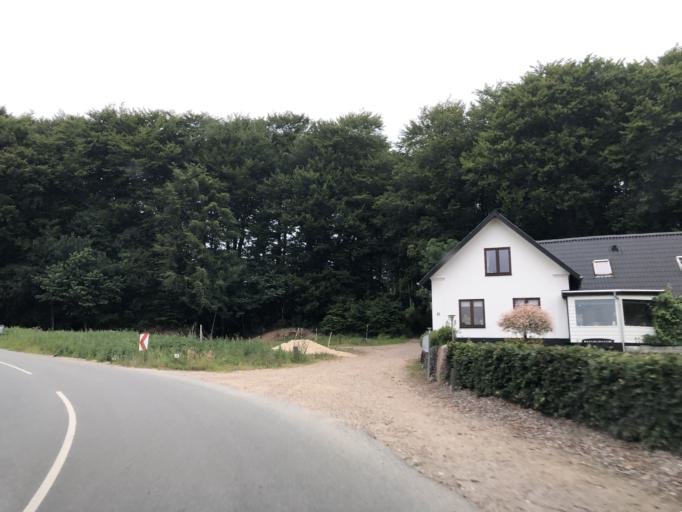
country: DK
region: South Denmark
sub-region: Vejle Kommune
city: Jelling
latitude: 55.7401
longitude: 9.4161
